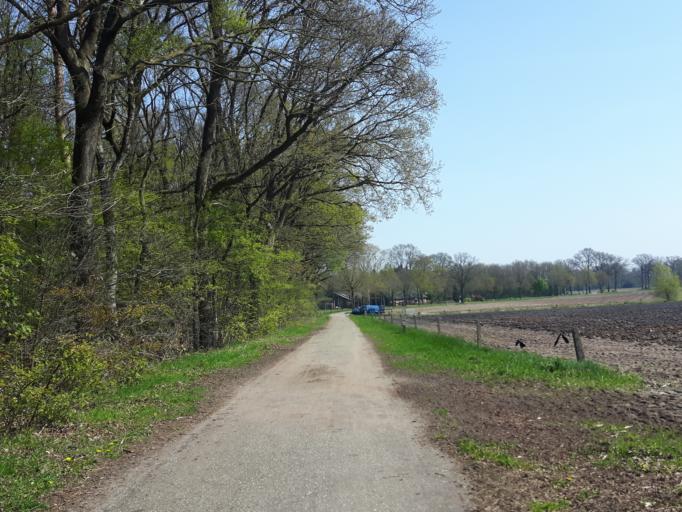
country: NL
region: Overijssel
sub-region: Gemeente Haaksbergen
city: Haaksbergen
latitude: 52.1416
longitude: 6.7925
